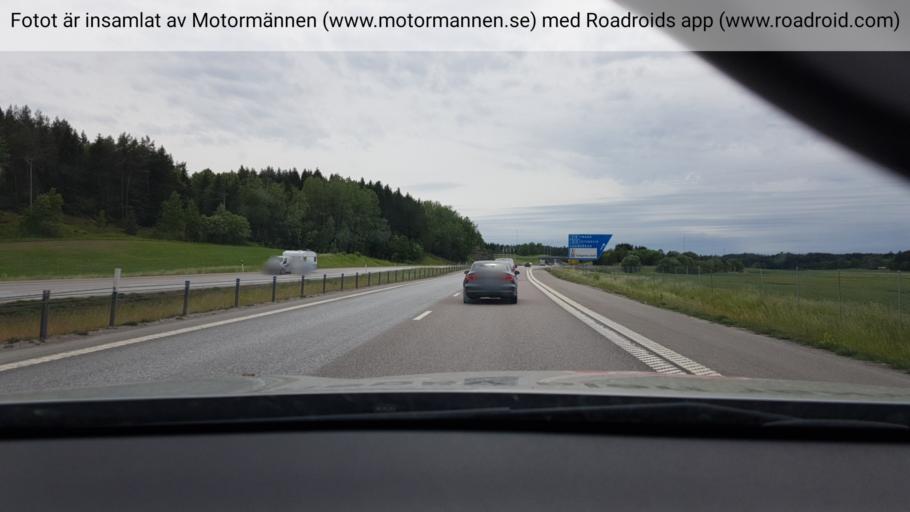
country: SE
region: Soedermanland
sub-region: Trosa Kommun
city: Vagnharad
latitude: 58.9642
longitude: 17.4964
